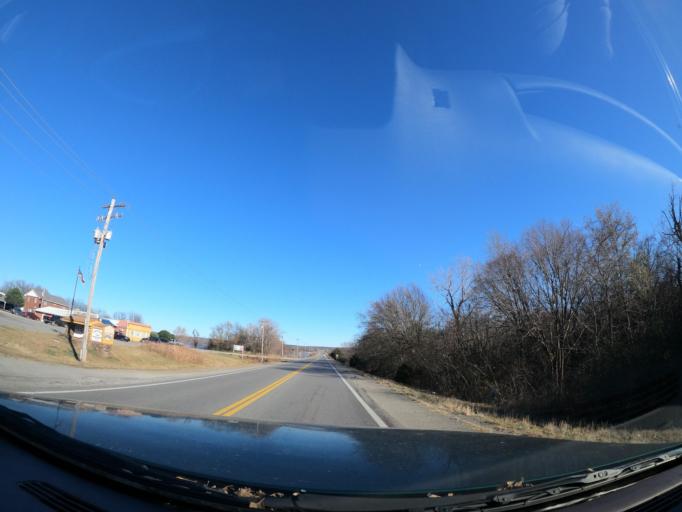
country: US
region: Oklahoma
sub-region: Pittsburg County
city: Longtown
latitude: 35.2392
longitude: -95.5124
